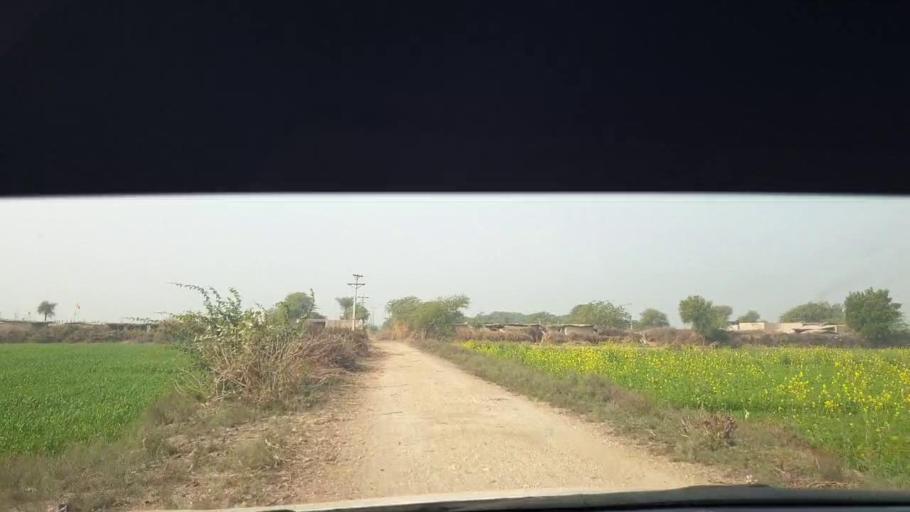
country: PK
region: Sindh
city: Berani
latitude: 25.7662
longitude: 68.7937
